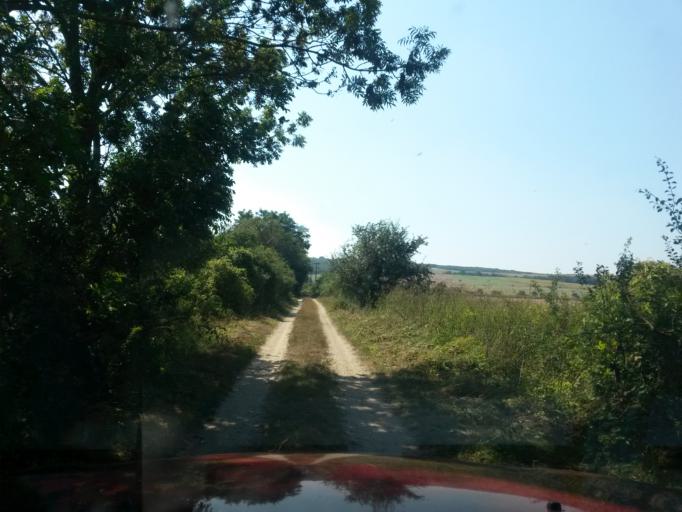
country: HU
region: Borsod-Abauj-Zemplen
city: Gonc
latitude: 48.5386
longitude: 21.1561
